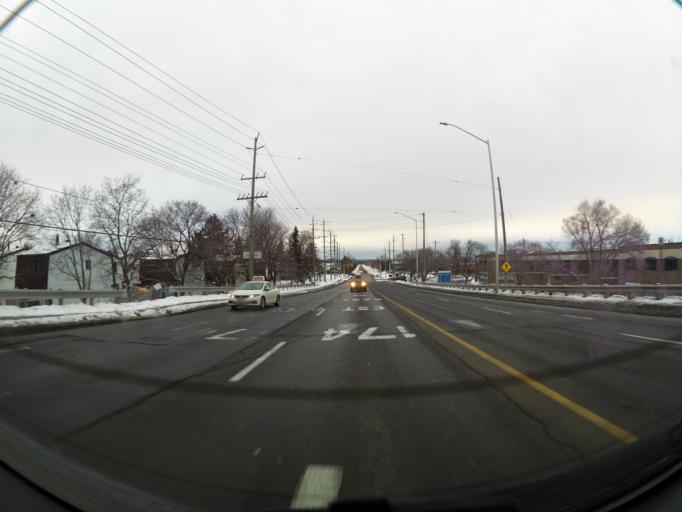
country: CA
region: Quebec
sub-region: Outaouais
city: Gatineau
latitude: 45.4511
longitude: -75.5888
